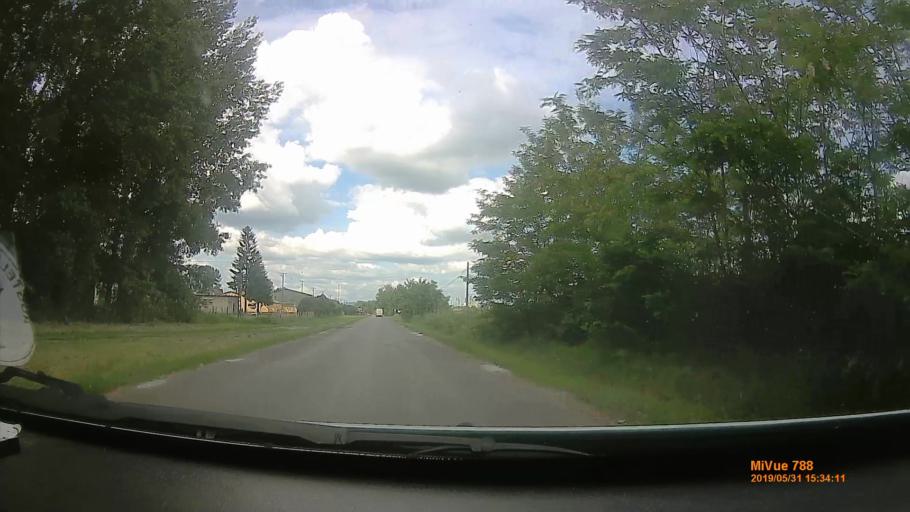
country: HU
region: Borsod-Abauj-Zemplen
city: Prugy
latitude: 48.0731
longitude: 21.2402
